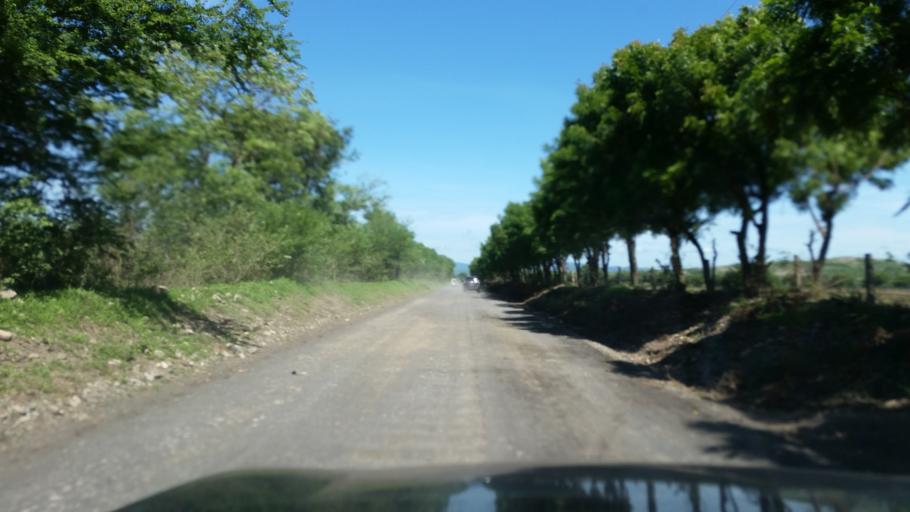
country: NI
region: Chinandega
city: Puerto Morazan
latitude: 12.7703
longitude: -87.0817
